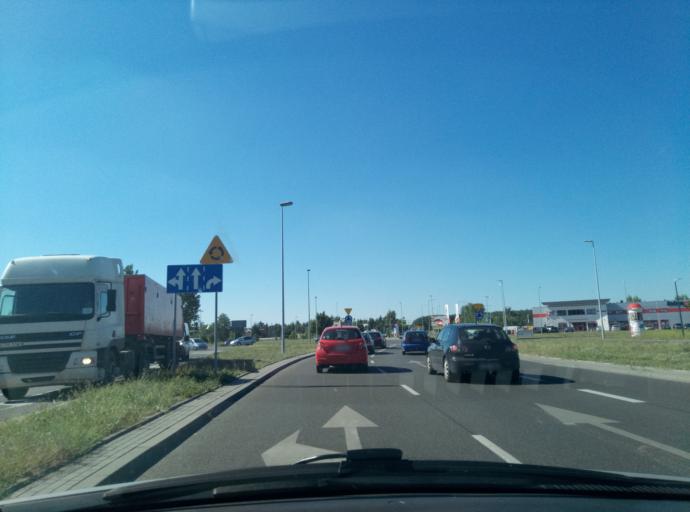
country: PL
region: Kujawsko-Pomorskie
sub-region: Torun
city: Torun
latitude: 53.0403
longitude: 18.5988
